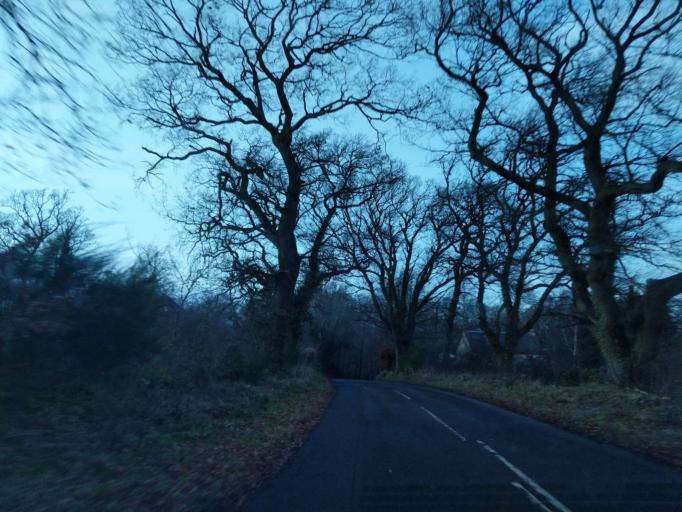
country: GB
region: Scotland
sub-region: Midlothian
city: Bonnyrigg
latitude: 55.8425
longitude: -3.0897
